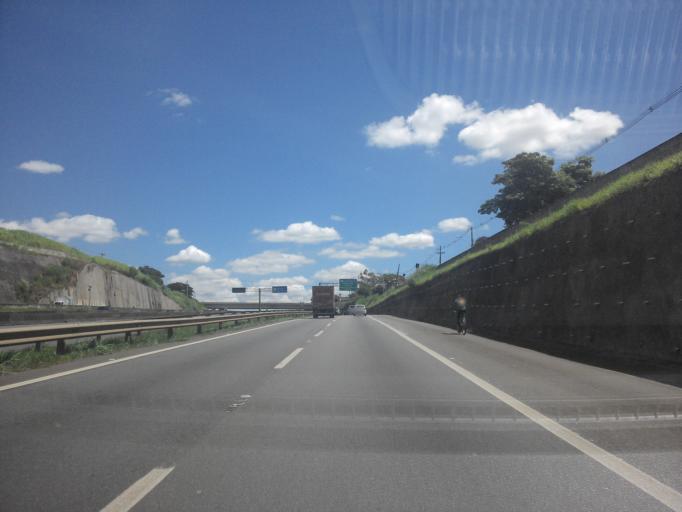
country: BR
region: Sao Paulo
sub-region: Campinas
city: Campinas
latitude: -22.8427
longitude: -47.0492
